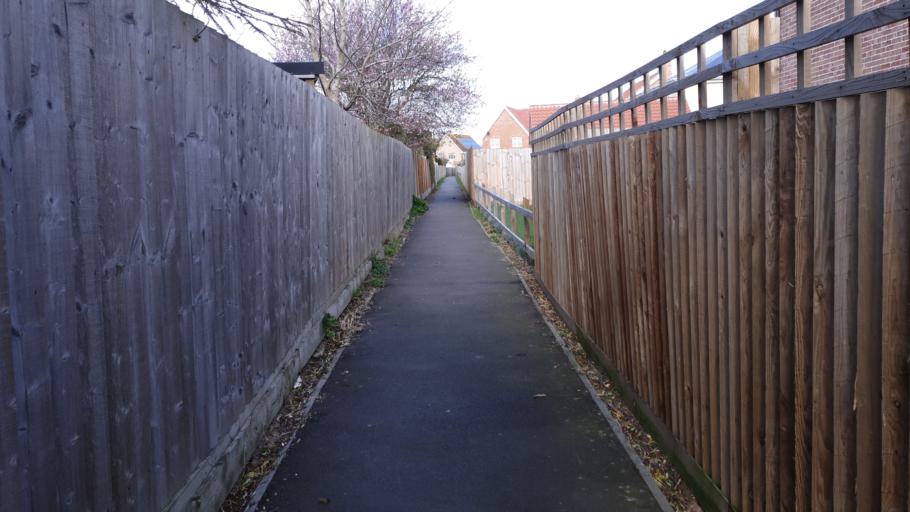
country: GB
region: England
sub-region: Essex
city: Brightlingsea
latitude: 51.8130
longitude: 1.0345
